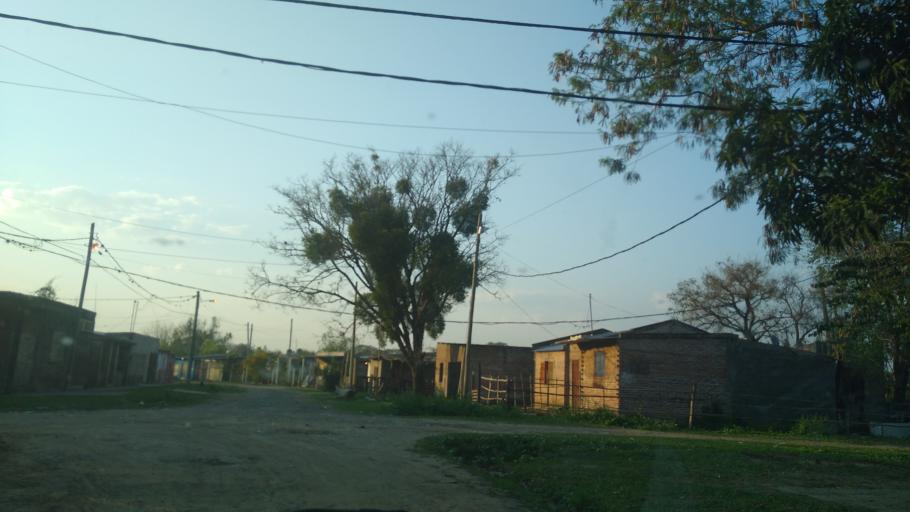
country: AR
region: Chaco
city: Barranqueras
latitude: -27.4716
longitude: -58.9564
